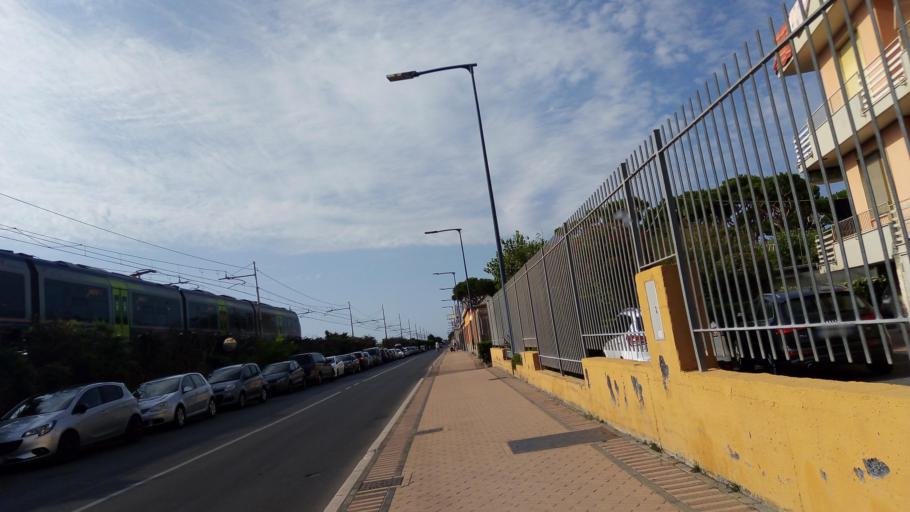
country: IT
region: Liguria
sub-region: Provincia di Savona
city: Ceriale
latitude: 44.0802
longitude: 8.2264
